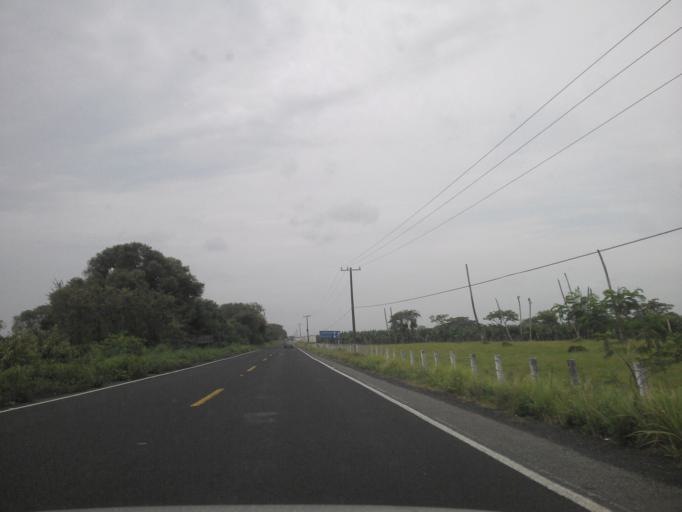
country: MX
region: Veracruz
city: Nautla
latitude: 20.2290
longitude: -96.7890
